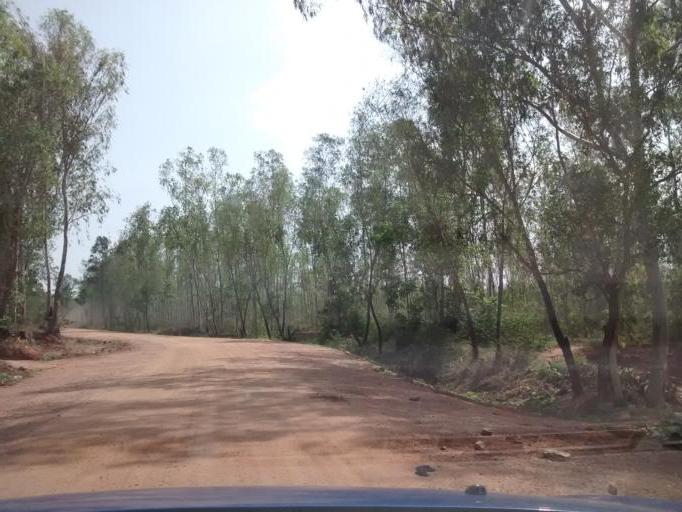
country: IN
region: Karnataka
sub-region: Hassan
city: Arkalgud
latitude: 12.7034
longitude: 76.1502
